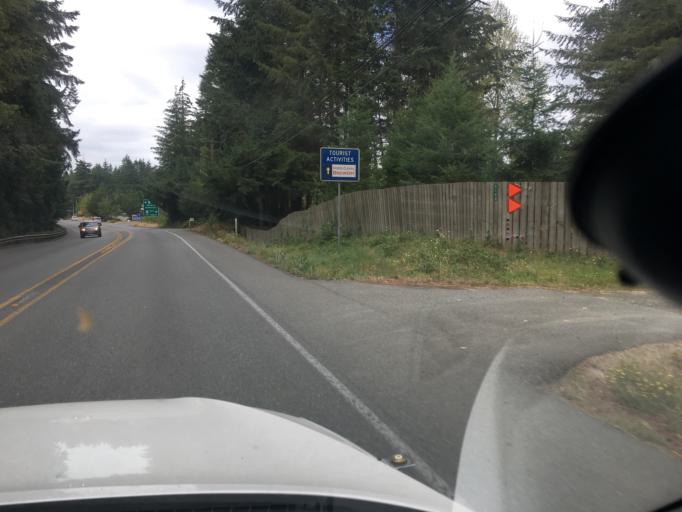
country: US
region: Washington
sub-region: Kitsap County
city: Kingston
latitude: 47.8052
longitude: -122.5661
